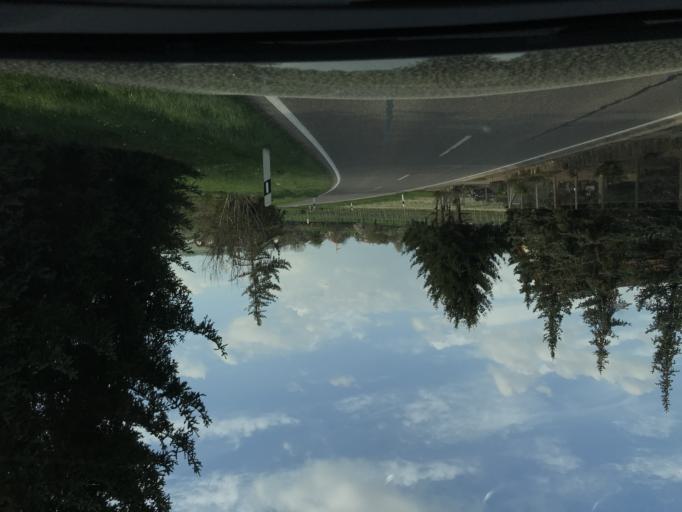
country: DE
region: Baden-Wuerttemberg
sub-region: Regierungsbezirk Stuttgart
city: Weinstadt-Endersbach
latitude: 48.7935
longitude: 9.3613
